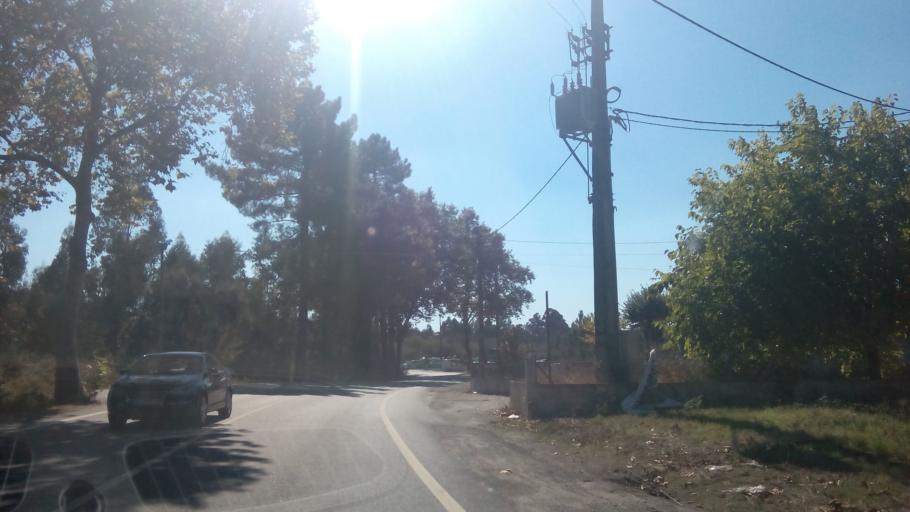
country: PT
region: Porto
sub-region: Lousada
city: Meinedo
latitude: 41.2514
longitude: -8.2159
